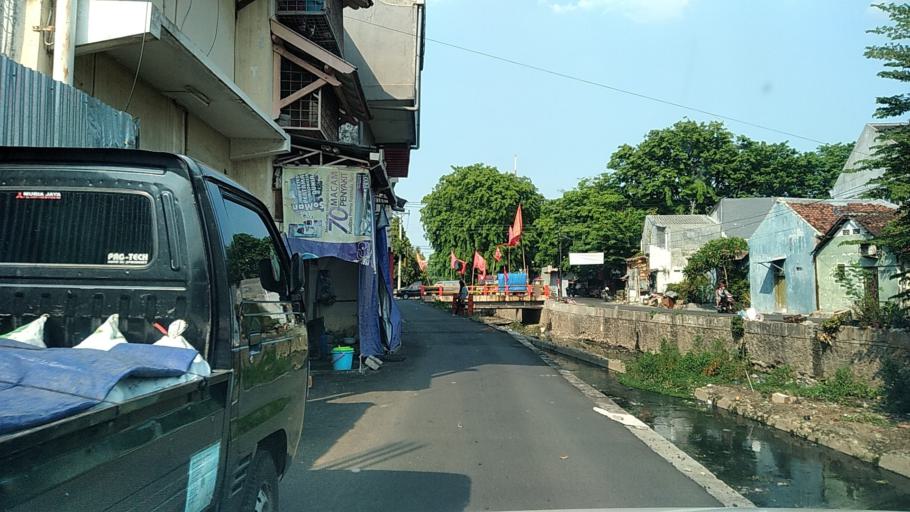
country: ID
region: Central Java
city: Semarang
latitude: -6.9777
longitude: 110.4276
